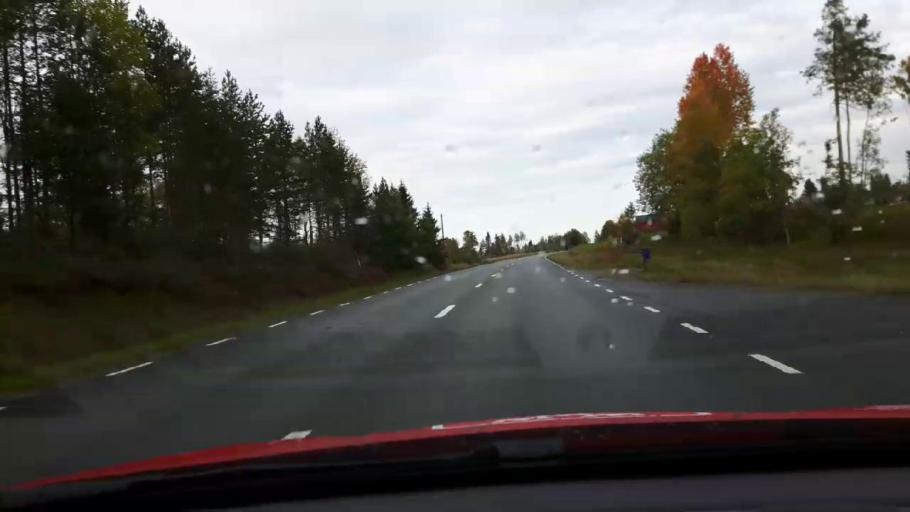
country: SE
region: Jaemtland
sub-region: Krokoms Kommun
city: Krokom
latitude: 63.1094
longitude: 14.2941
